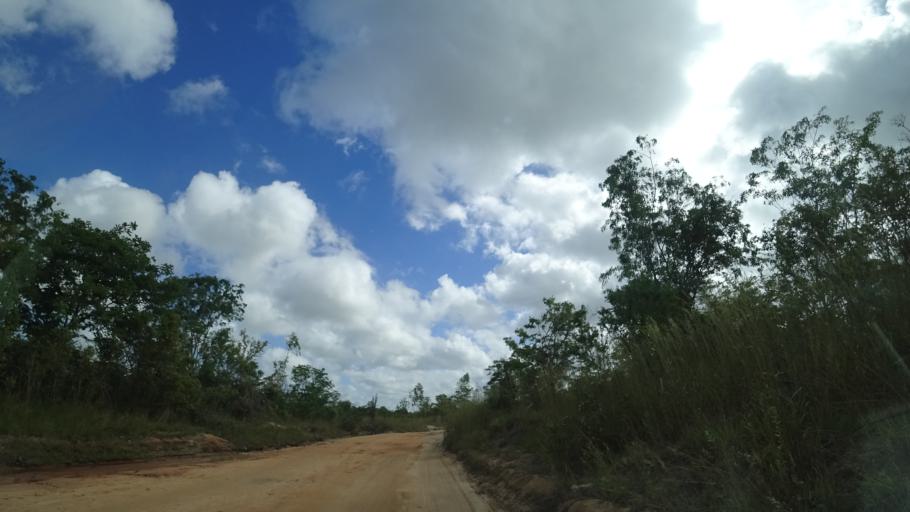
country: MZ
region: Sofala
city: Dondo
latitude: -19.4381
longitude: 34.7139
